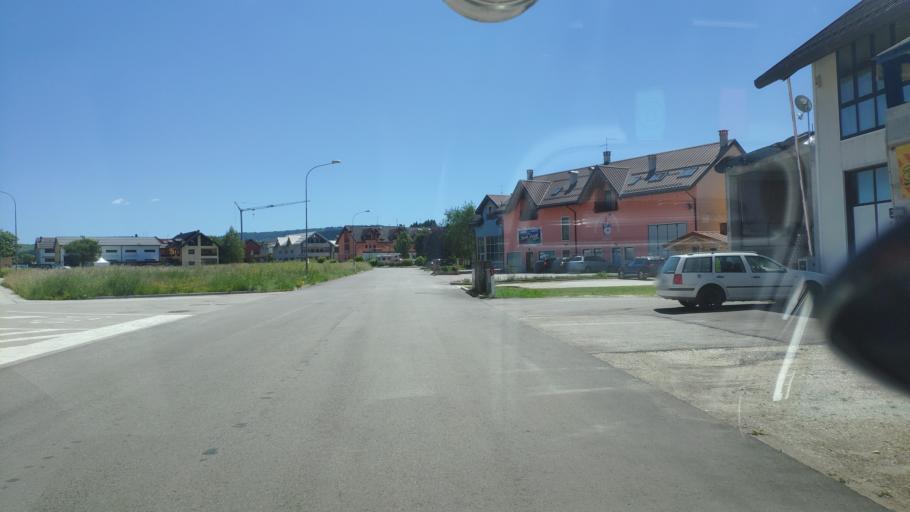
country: IT
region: Veneto
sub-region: Provincia di Vicenza
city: Canove di Roana
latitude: 45.8593
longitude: 11.4859
